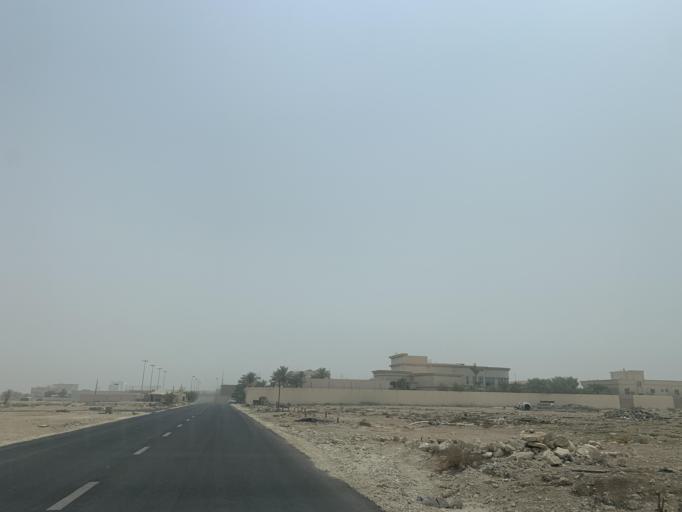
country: BH
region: Central Governorate
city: Madinat Hamad
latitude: 26.1686
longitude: 50.4817
